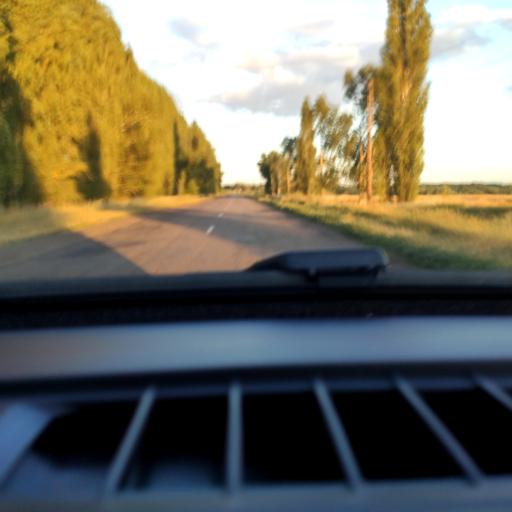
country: RU
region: Voronezj
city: Orlovo
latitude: 51.6176
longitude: 39.7911
